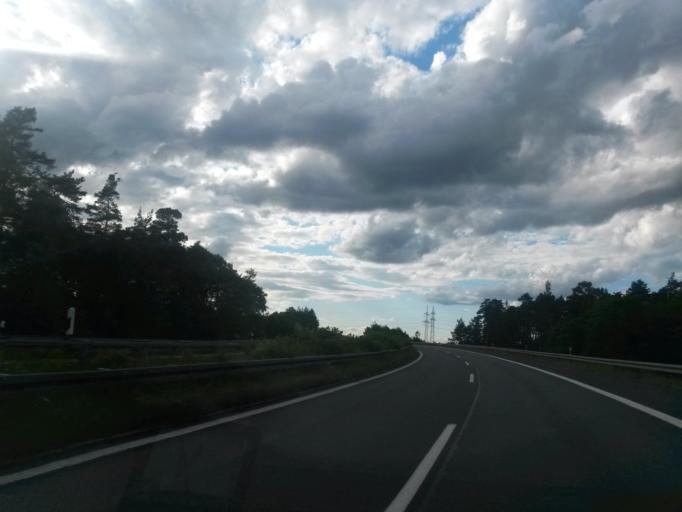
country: DE
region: Bavaria
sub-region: Regierungsbezirk Mittelfranken
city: Feucht
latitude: 49.3479
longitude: 11.2056
